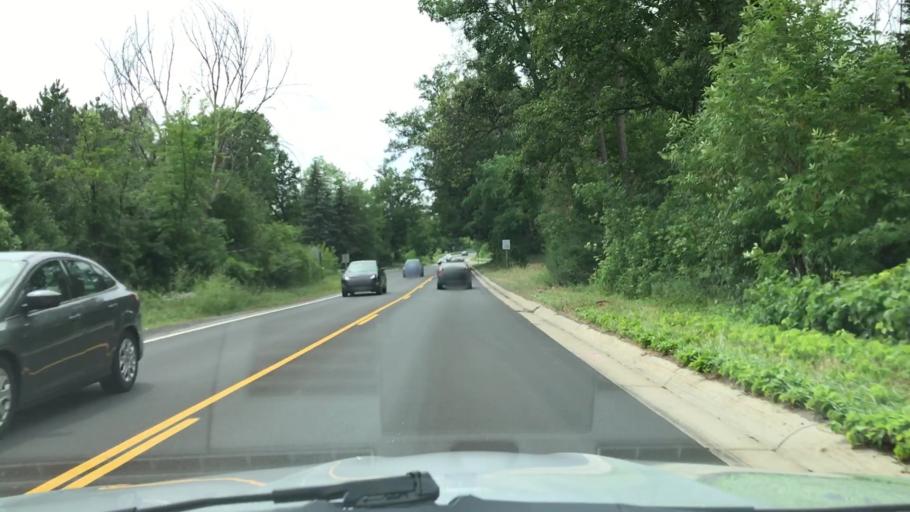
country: US
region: Michigan
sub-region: Oakland County
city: West Bloomfield Township
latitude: 42.5717
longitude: -83.3799
